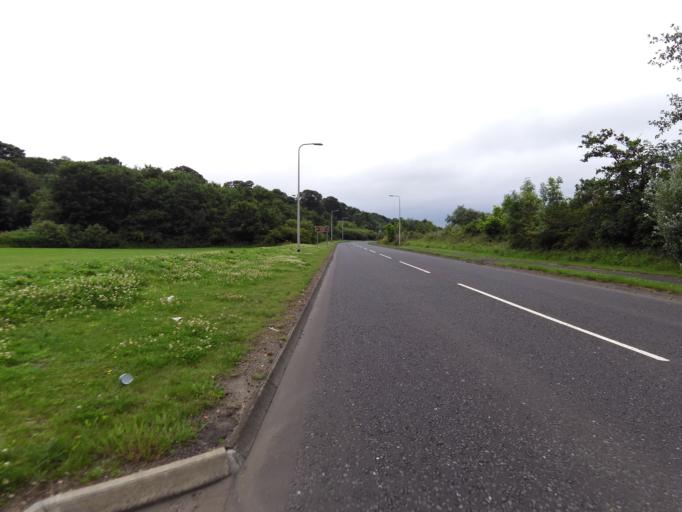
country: GB
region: Scotland
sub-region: East Lothian
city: Prestonpans
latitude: 55.9510
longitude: -3.0110
